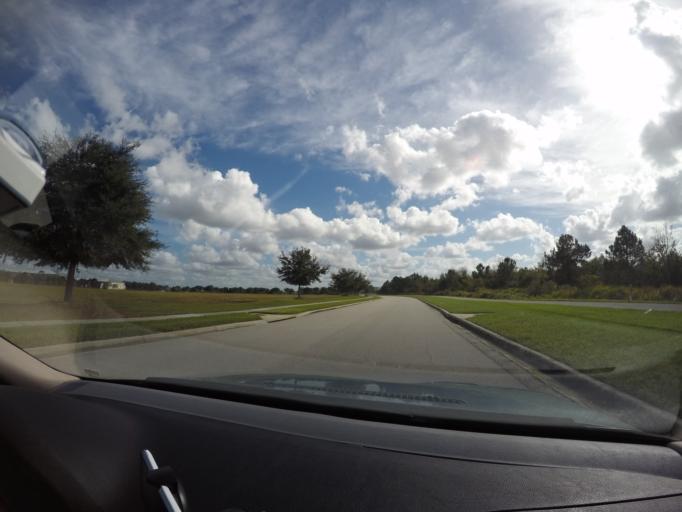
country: US
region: Florida
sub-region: Orange County
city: Wedgefield
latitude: 28.4131
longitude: -81.2061
